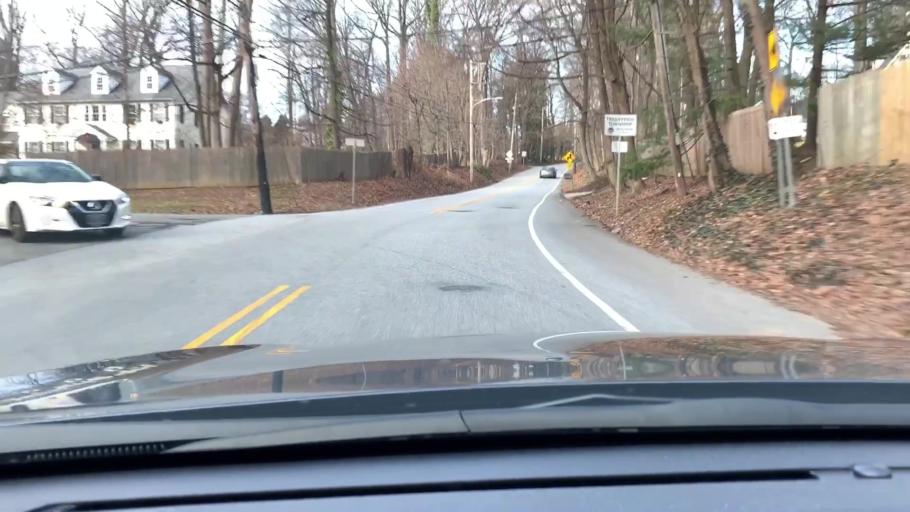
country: US
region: Pennsylvania
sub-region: Chester County
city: Paoli
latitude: 40.0366
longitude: -75.4778
